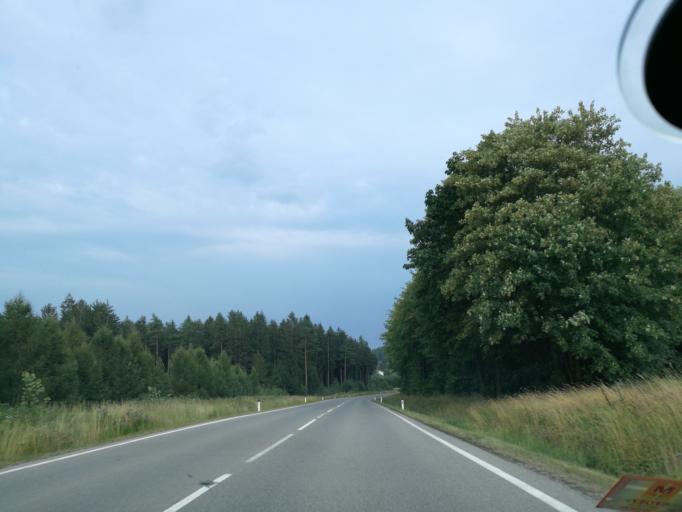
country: AT
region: Lower Austria
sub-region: Politischer Bezirk Gmund
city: Heidenreichstein
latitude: 48.8594
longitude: 15.1407
